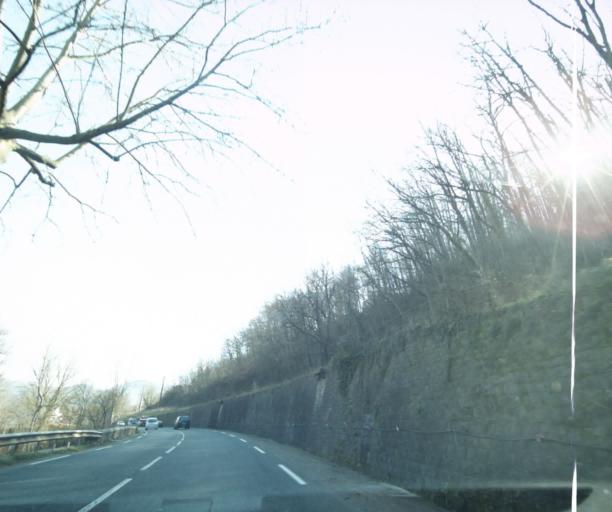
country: FR
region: Midi-Pyrenees
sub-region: Departement de l'Aveyron
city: Saint-Affrique
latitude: 43.9563
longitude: 2.8650
